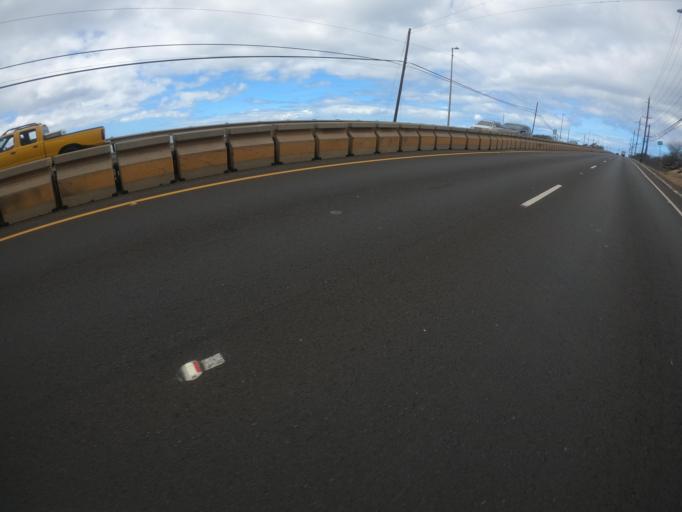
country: US
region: Hawaii
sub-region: Honolulu County
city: Ma'ili
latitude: 21.3996
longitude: -158.1733
